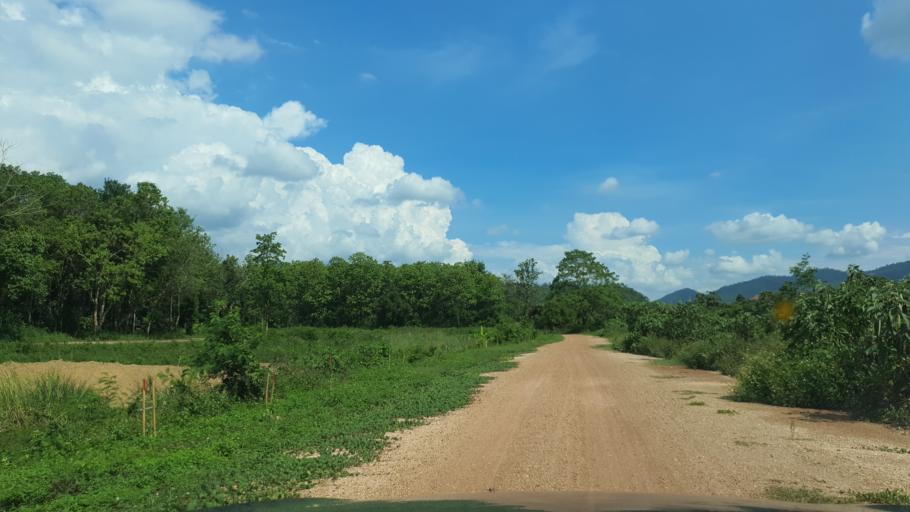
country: TH
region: Chiang Mai
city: Mae Taeng
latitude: 19.0909
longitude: 99.0784
